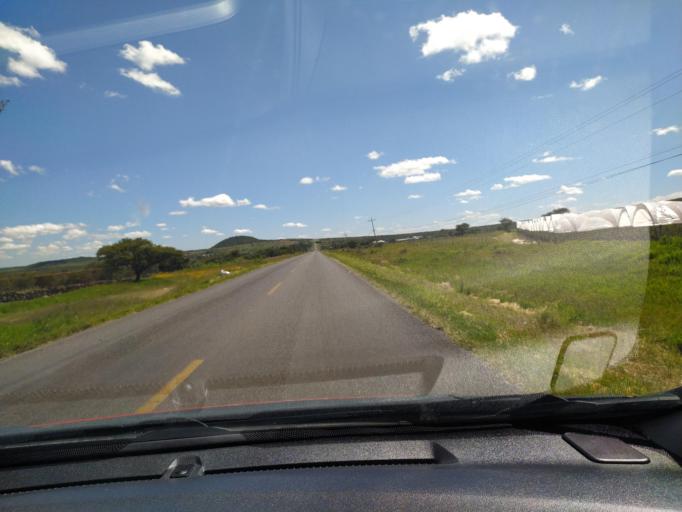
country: MX
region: Jalisco
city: San Miguel el Alto
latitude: 21.0183
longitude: -102.4620
